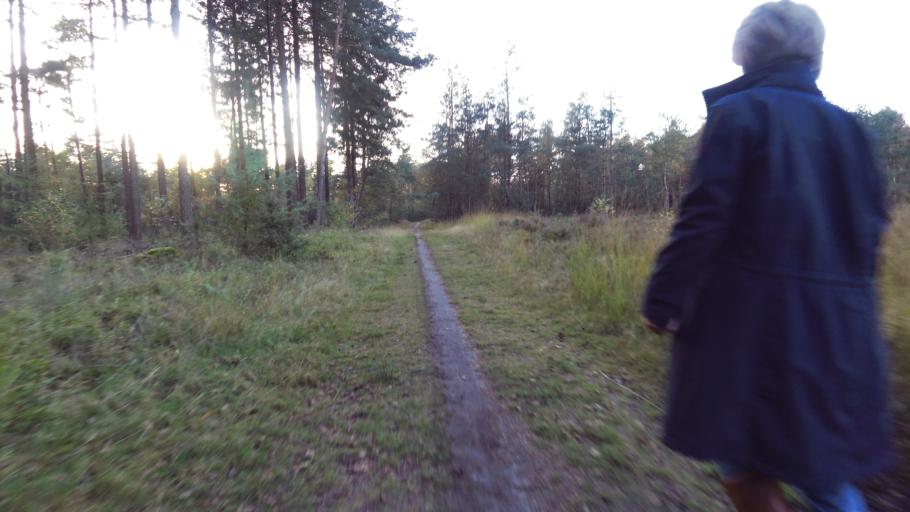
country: NL
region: Gelderland
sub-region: Gemeente Epe
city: Epe
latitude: 52.3765
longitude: 5.9530
